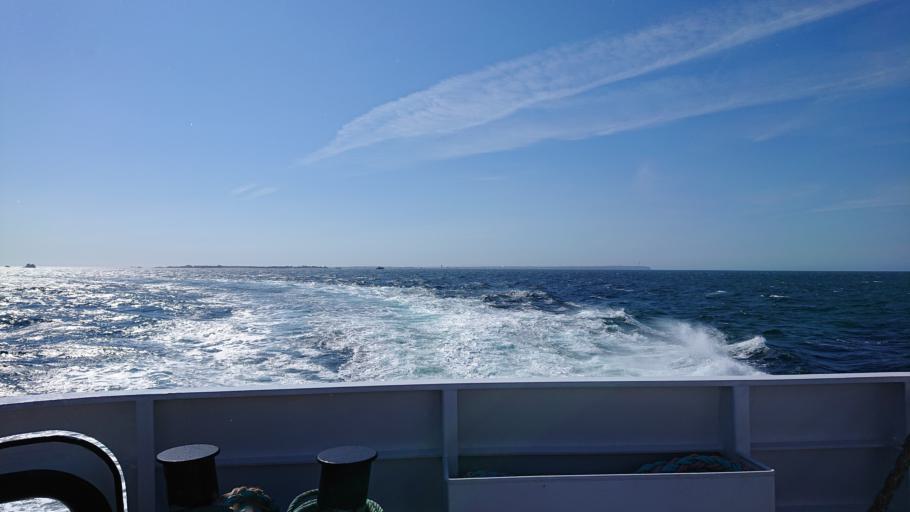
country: FR
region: Brittany
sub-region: Departement du Finistere
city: Le Conquet
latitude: 48.4154
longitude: -4.9426
